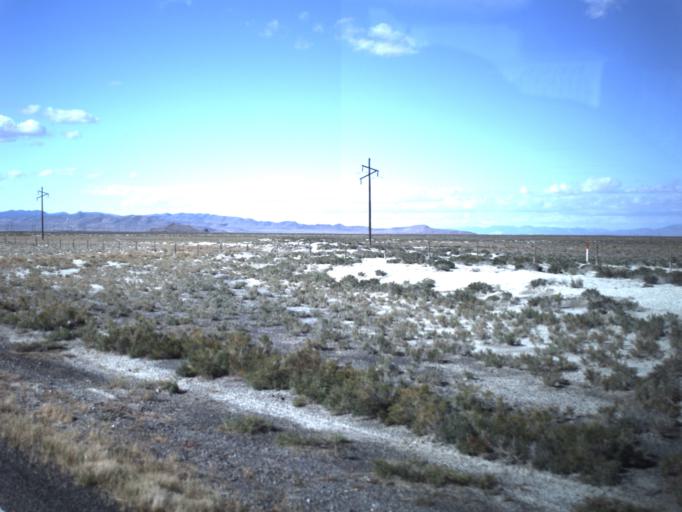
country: US
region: Utah
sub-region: Millard County
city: Delta
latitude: 39.1676
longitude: -112.7083
